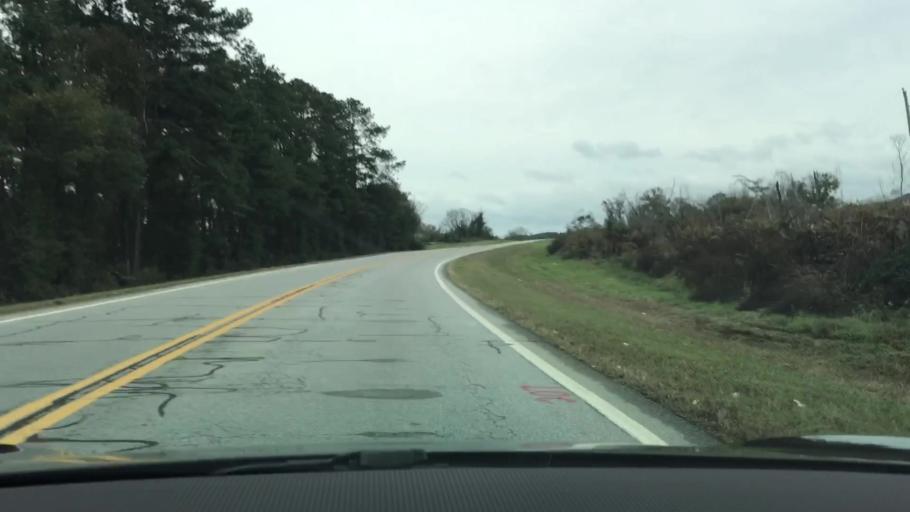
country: US
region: Georgia
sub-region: Warren County
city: Warrenton
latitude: 33.3741
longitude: -82.6031
